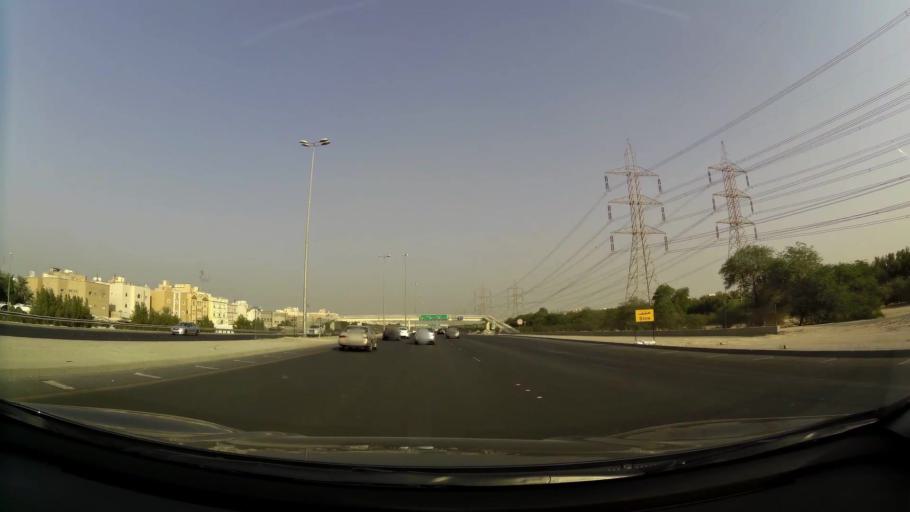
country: KW
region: Al Asimah
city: Ar Rabiyah
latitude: 29.2969
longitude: 47.8833
